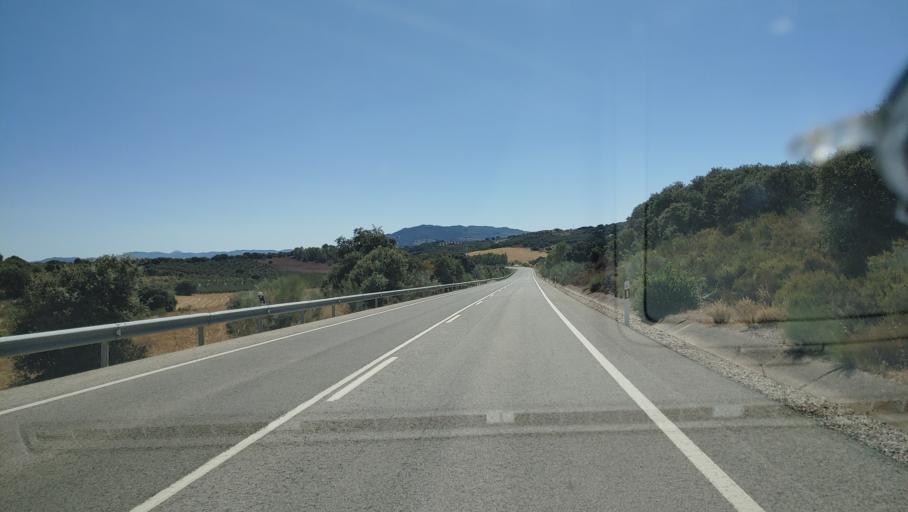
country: ES
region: Andalusia
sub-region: Provincia de Jaen
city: Genave
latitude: 38.4627
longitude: -2.7629
